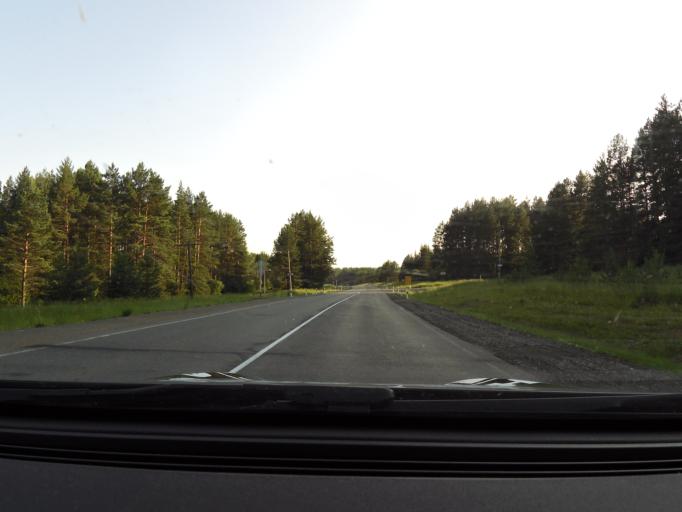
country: RU
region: Sverdlovsk
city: Nizhniye Sergi
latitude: 56.6355
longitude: 59.2467
